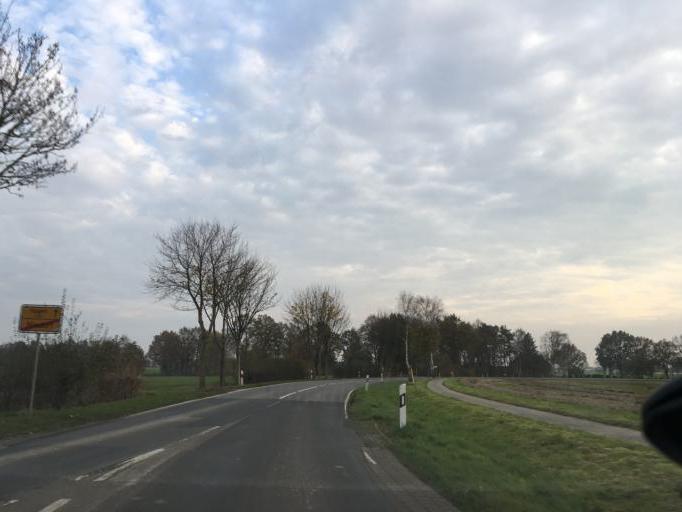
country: DE
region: Lower Saxony
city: Bergen
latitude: 52.8379
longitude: 9.9768
